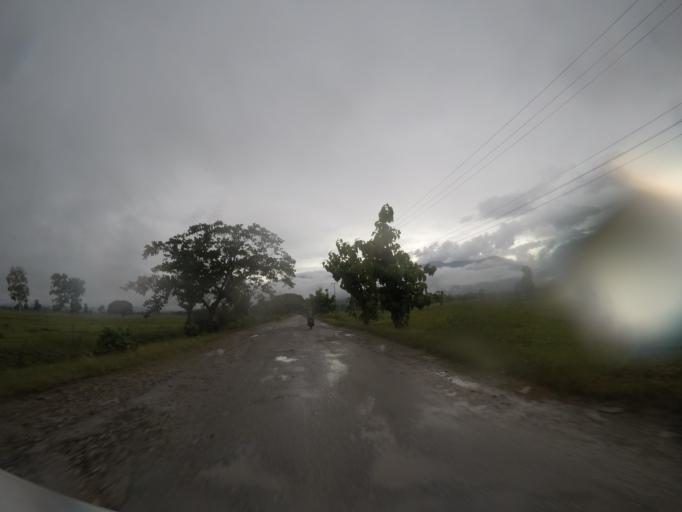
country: TL
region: Bobonaro
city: Maliana
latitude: -8.9903
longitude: 125.1711
